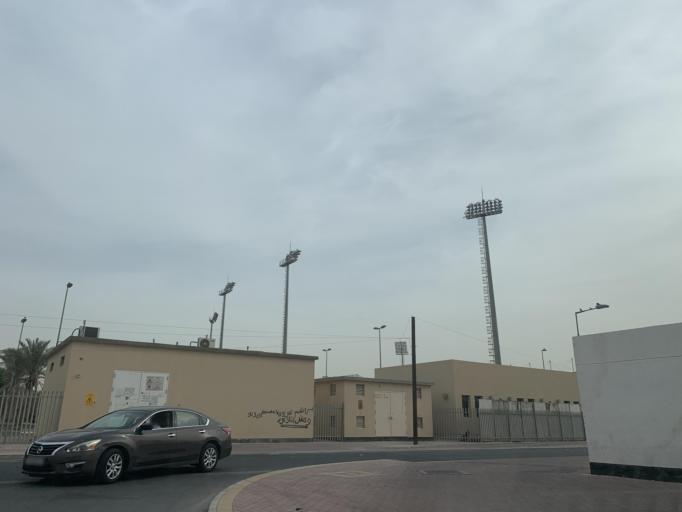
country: BH
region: Northern
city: Madinat `Isa
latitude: 26.1767
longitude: 50.5492
